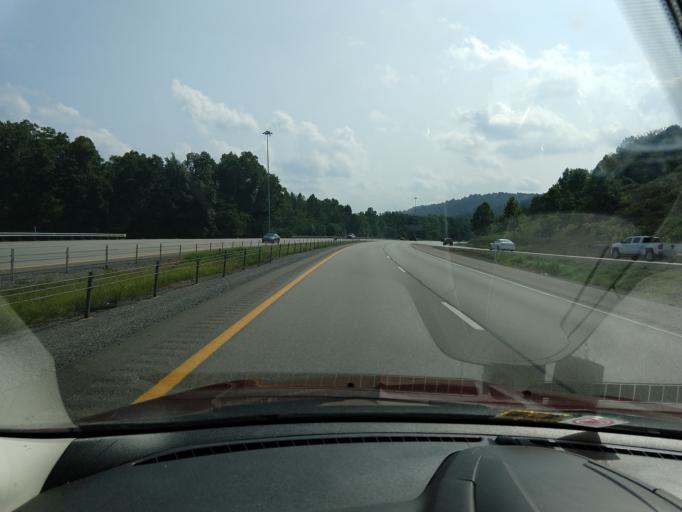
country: US
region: West Virginia
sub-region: Monongalia County
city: Morgantown
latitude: 39.5679
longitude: -79.9815
